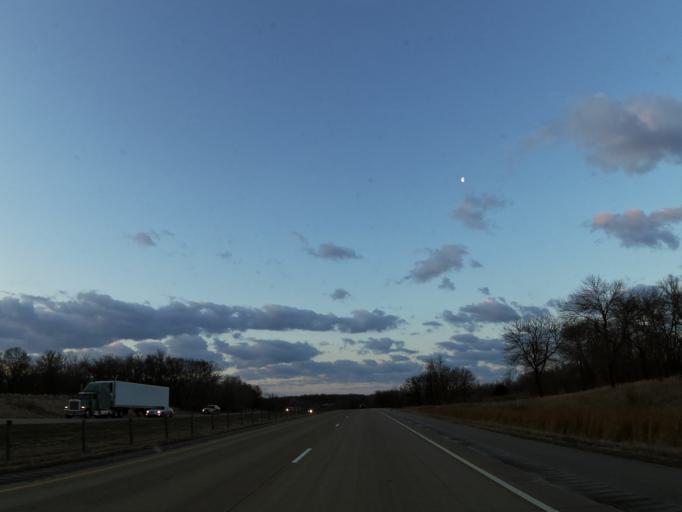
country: US
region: Minnesota
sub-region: Scott County
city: Elko New Market
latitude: 44.5383
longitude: -93.3015
